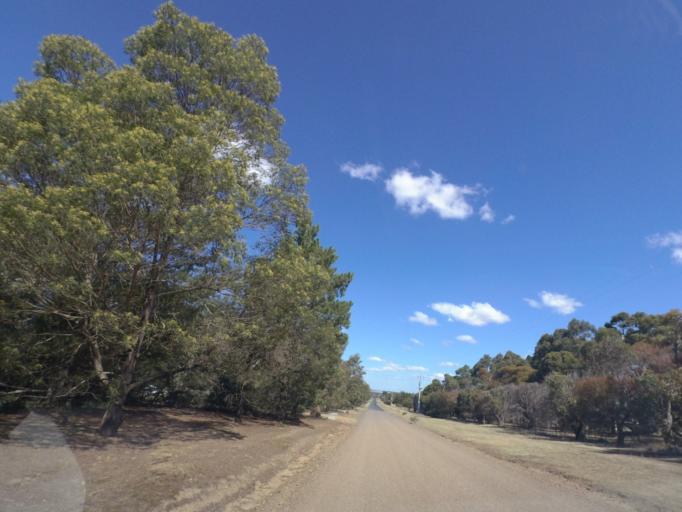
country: AU
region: Victoria
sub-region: Hume
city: Sunbury
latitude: -37.4552
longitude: 144.6620
